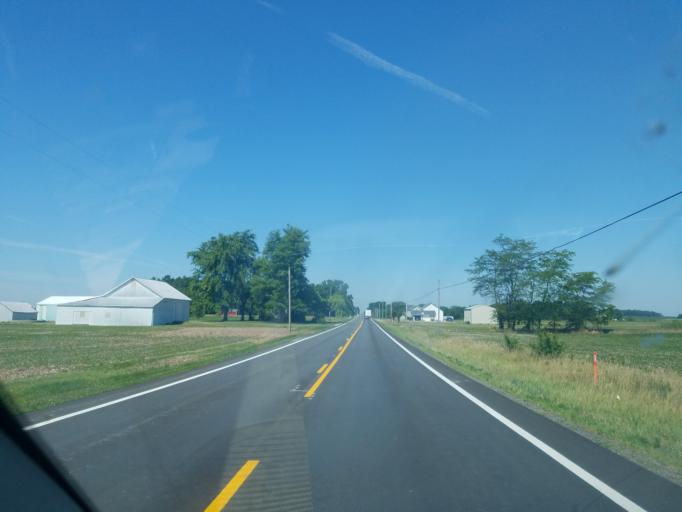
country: US
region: Ohio
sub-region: Shelby County
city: Jackson Center
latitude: 40.4395
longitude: -84.0861
